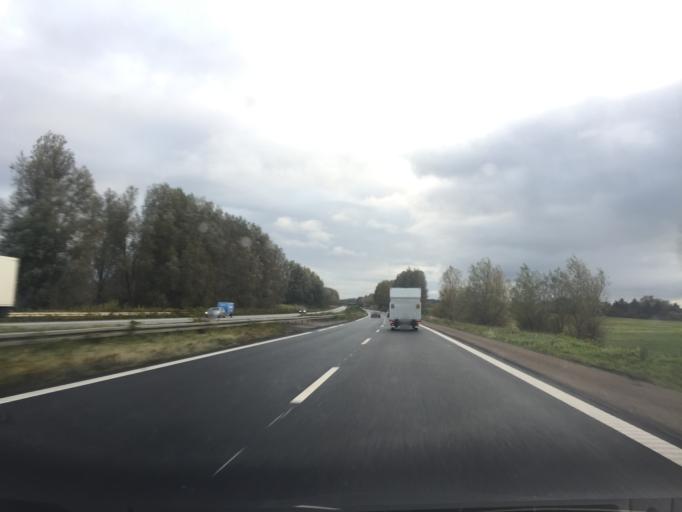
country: DK
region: Capital Region
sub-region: Fredensborg Kommune
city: Niva
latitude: 55.9486
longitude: 12.4781
